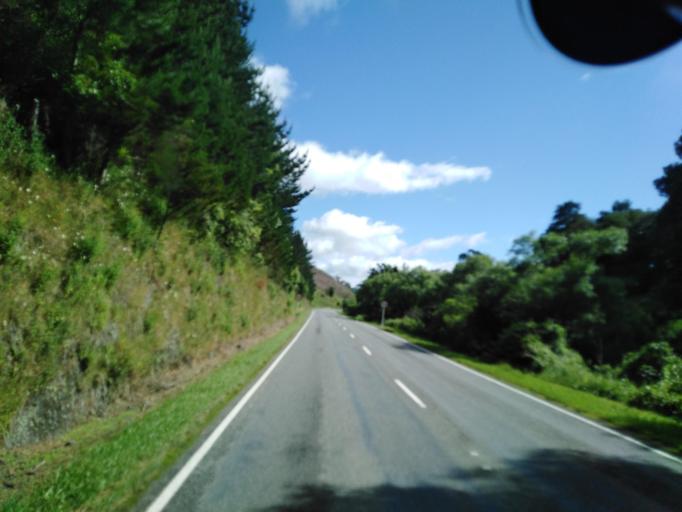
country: NZ
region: Nelson
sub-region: Nelson City
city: Nelson
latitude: -41.2576
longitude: 173.5759
